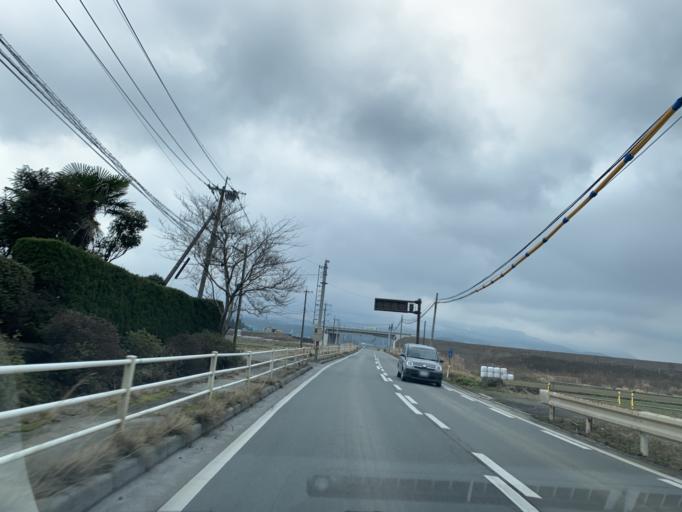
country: JP
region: Kumamoto
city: Aso
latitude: 32.9167
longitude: 130.9797
